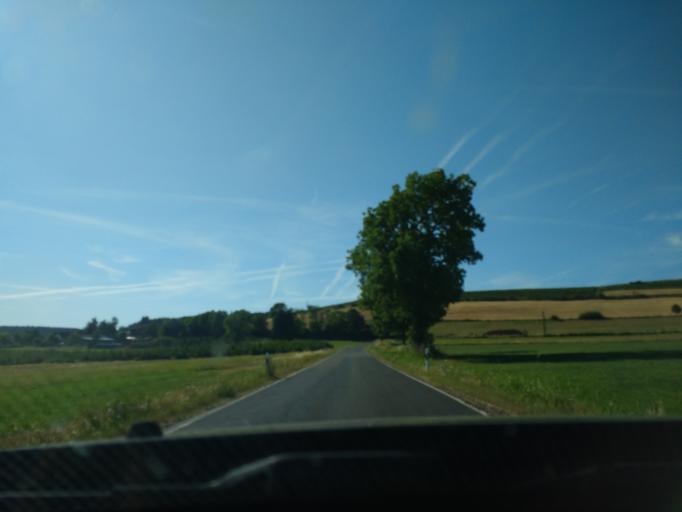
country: DE
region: Rheinland-Pfalz
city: Salm
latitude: 50.1492
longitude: 6.6993
